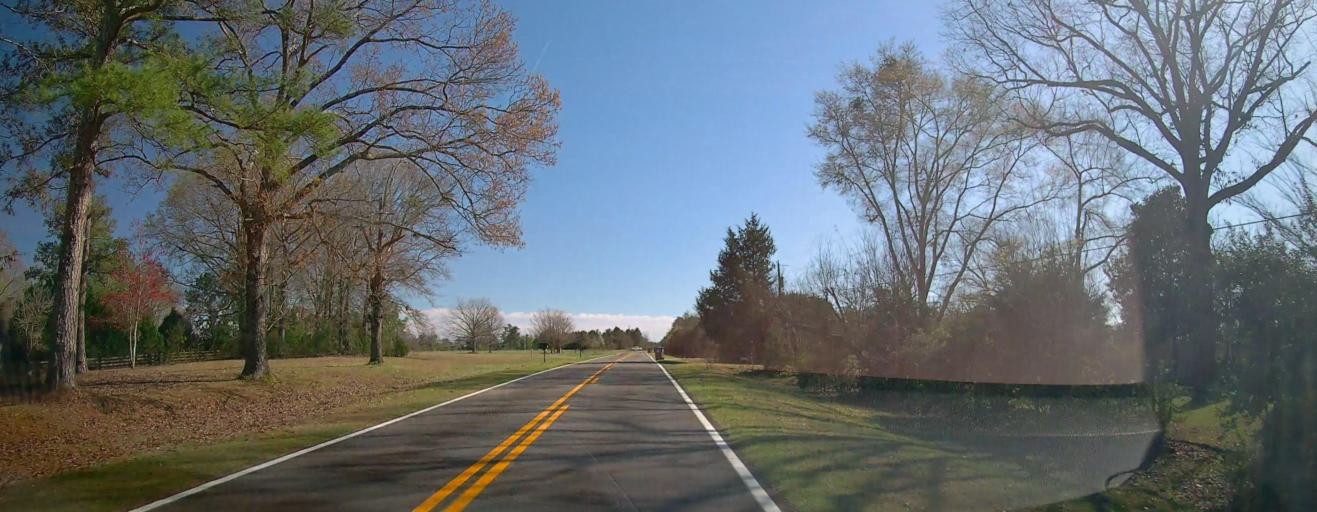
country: US
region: Georgia
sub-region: Peach County
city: Fort Valley
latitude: 32.6144
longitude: -83.8949
